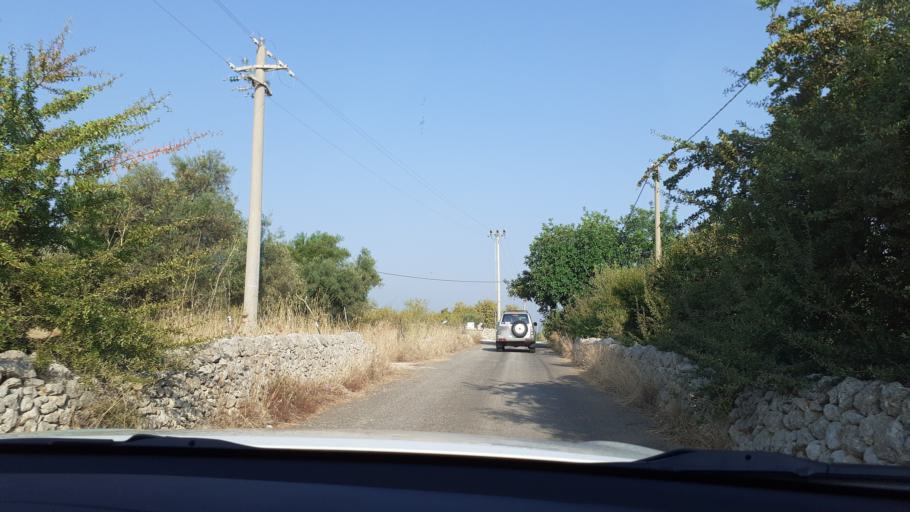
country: IT
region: Sicily
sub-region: Provincia di Siracusa
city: Cassibile
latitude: 36.9822
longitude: 15.1644
